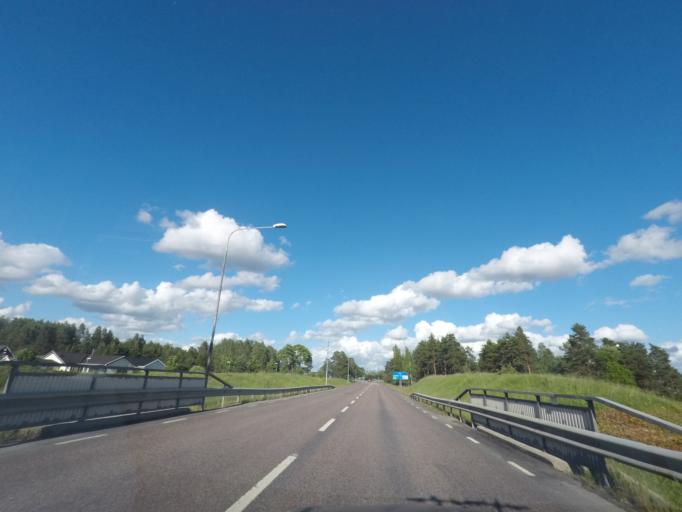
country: SE
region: Vaestmanland
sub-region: Arboga Kommun
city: Arboga
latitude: 59.4044
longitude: 15.8272
